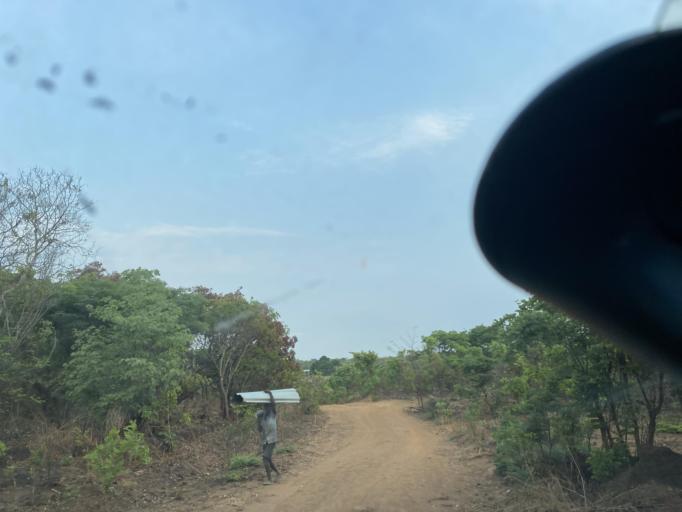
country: ZM
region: Lusaka
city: Chongwe
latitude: -15.2079
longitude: 28.5032
